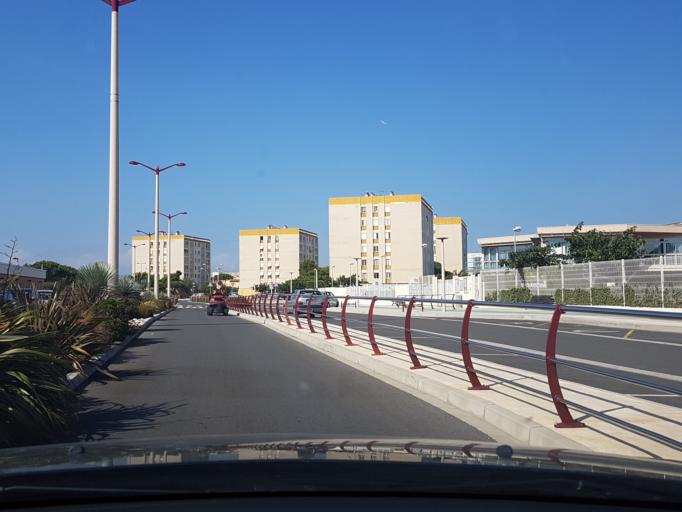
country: FR
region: Languedoc-Roussillon
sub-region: Departement de l'Aude
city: Port-la-Nouvelle
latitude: 43.0166
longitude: 3.0497
